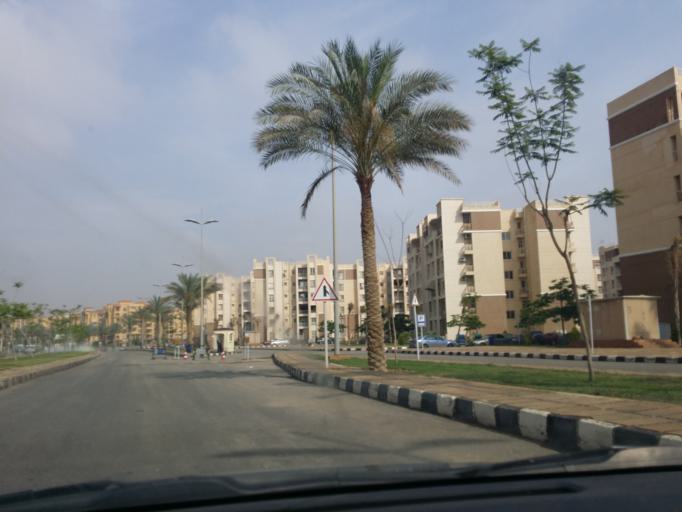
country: EG
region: Muhafazat al Qalyubiyah
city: Al Khankah
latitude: 30.0844
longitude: 31.6461
